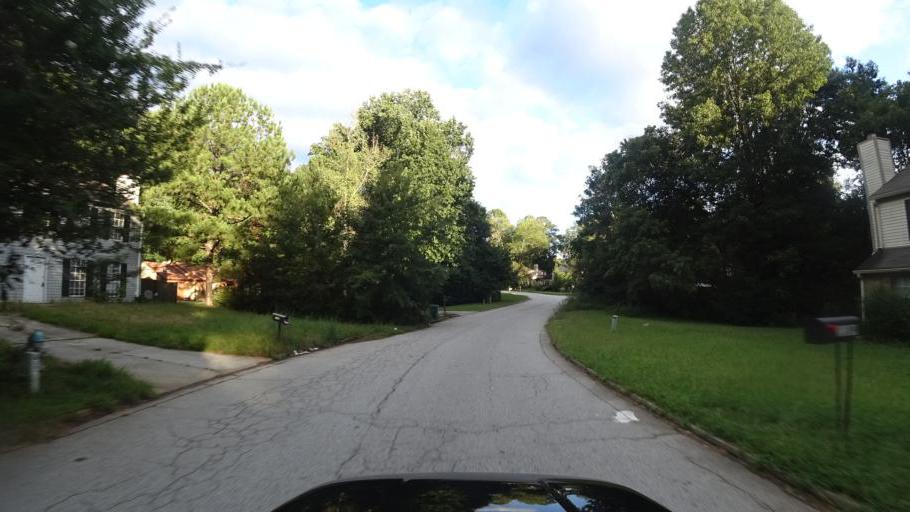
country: US
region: Georgia
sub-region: DeKalb County
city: Stone Mountain
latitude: 33.7593
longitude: -84.1861
